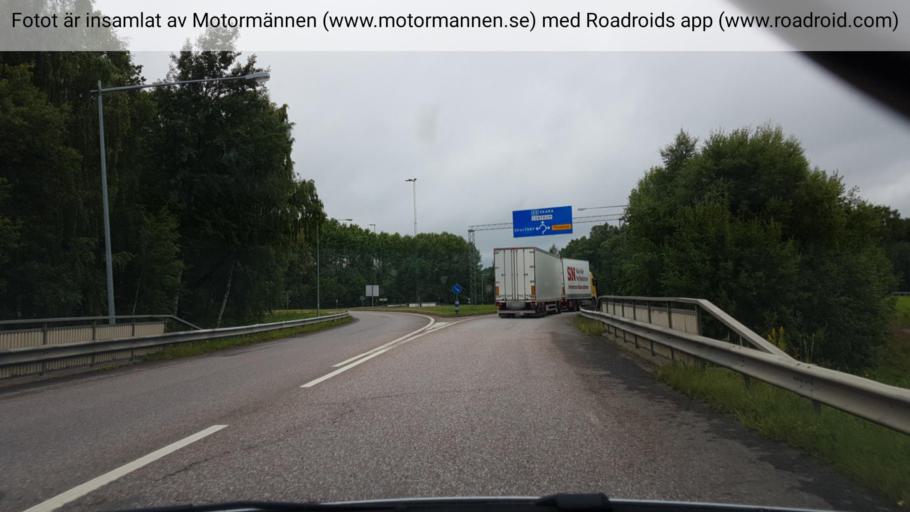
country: SE
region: Vaestra Goetaland
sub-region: Skovde Kommun
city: Skultorp
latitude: 58.3687
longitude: 13.8396
